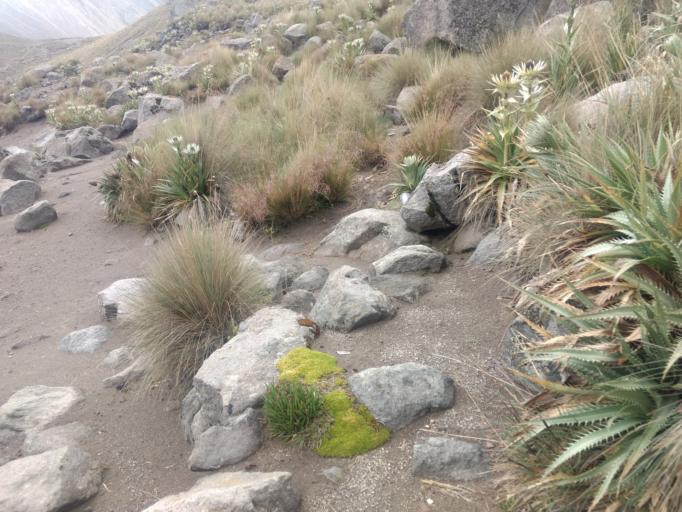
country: MX
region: Mexico
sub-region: Tenango del Valle
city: Santa Cruz Pueblo Nuevo (Pueblo Nuevo)
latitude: 19.1081
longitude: -99.7527
